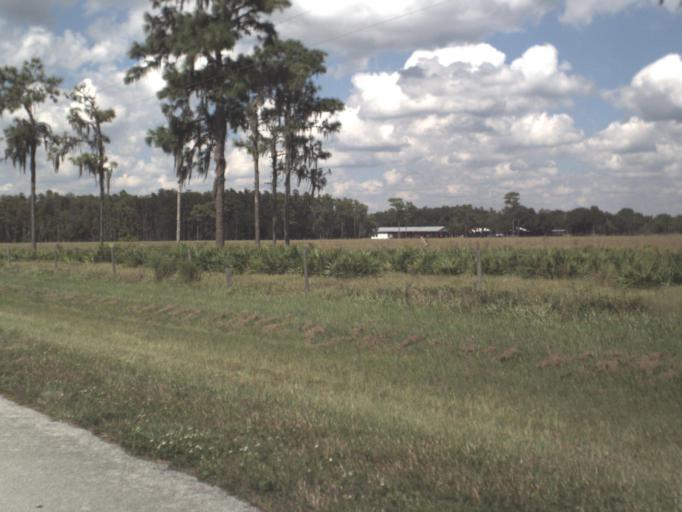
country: US
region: Florida
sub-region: Hardee County
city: Zolfo Springs
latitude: 27.4454
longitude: -81.6223
